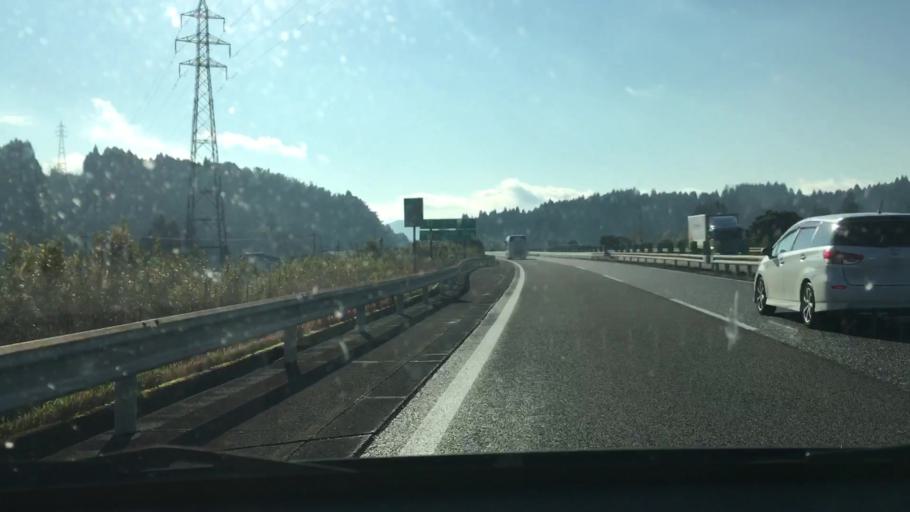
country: JP
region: Kagoshima
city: Okuchi-shinohara
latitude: 32.0222
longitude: 130.7762
